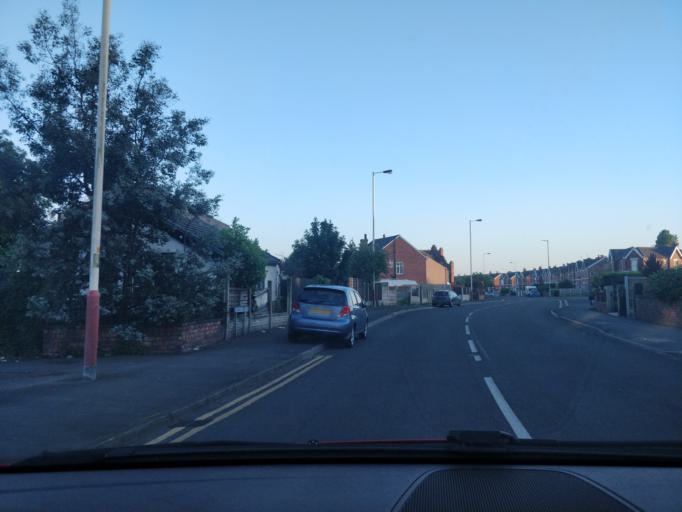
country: GB
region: England
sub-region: Sefton
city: Southport
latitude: 53.6534
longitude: -2.9656
